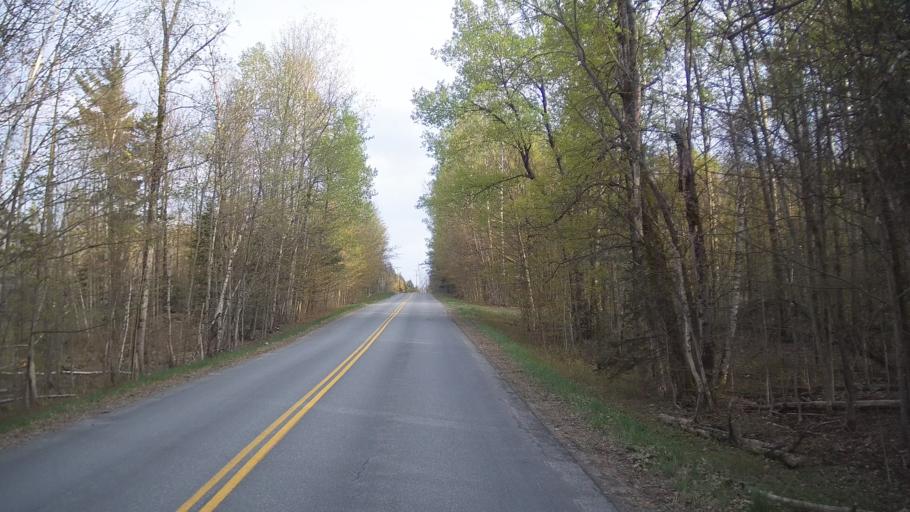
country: US
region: Vermont
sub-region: Orleans County
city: Newport
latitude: 44.9385
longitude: -72.4367
